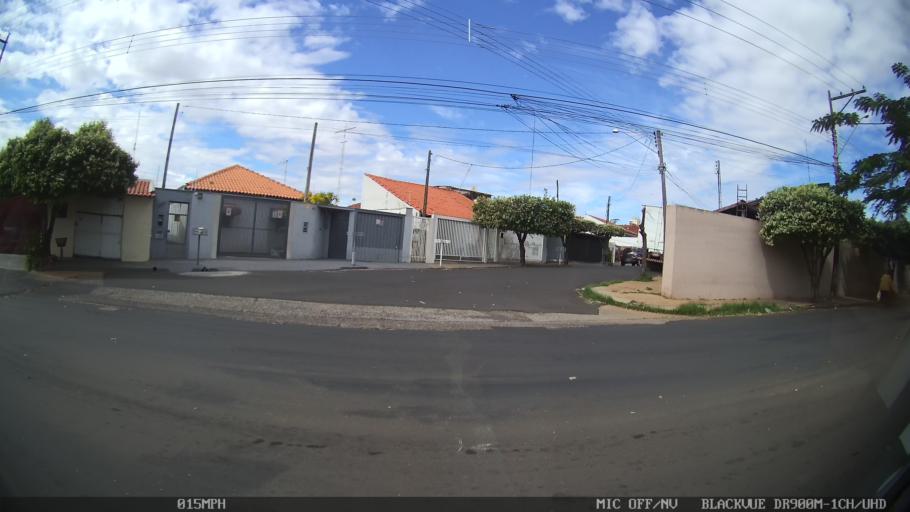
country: BR
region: Sao Paulo
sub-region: Bady Bassitt
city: Bady Bassitt
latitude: -20.8100
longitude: -49.5144
